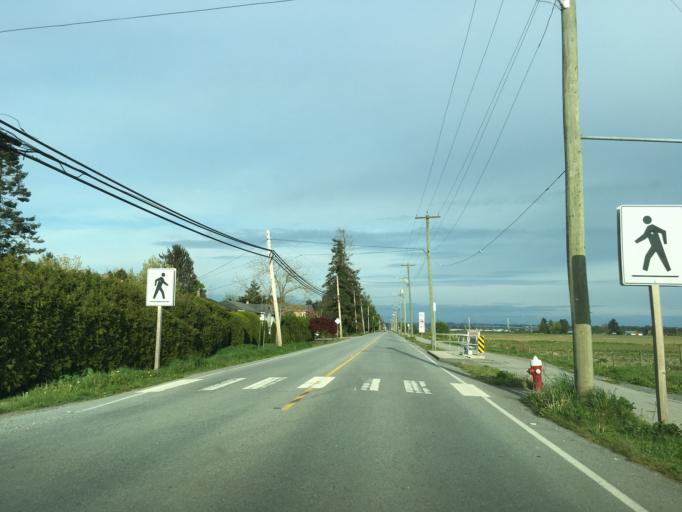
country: CA
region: British Columbia
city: Ladner
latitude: 49.1699
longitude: -123.0357
